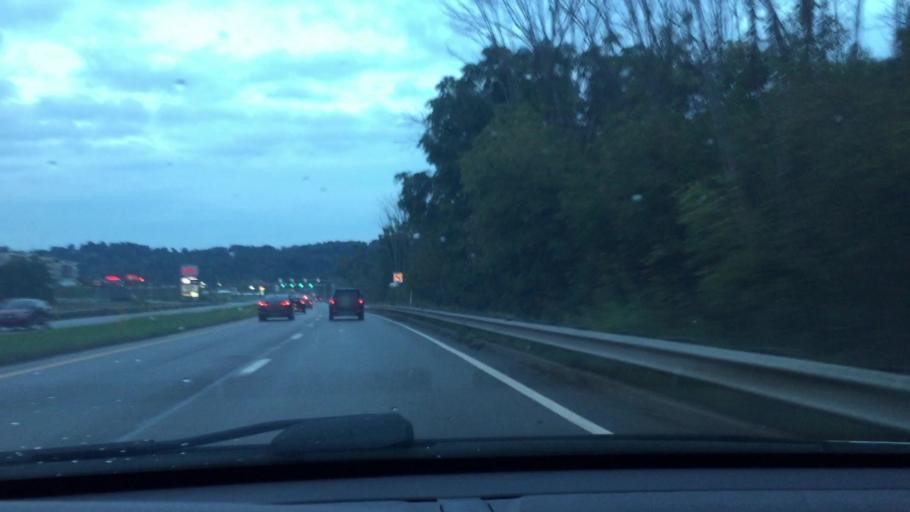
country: US
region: Pennsylvania
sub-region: Washington County
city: McGovern
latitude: 40.2185
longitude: -80.2049
